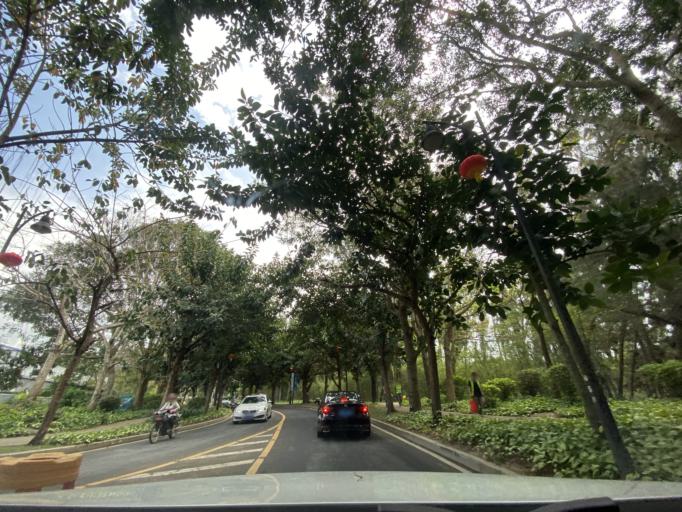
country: CN
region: Hainan
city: Liji
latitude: 18.6695
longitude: 110.2666
